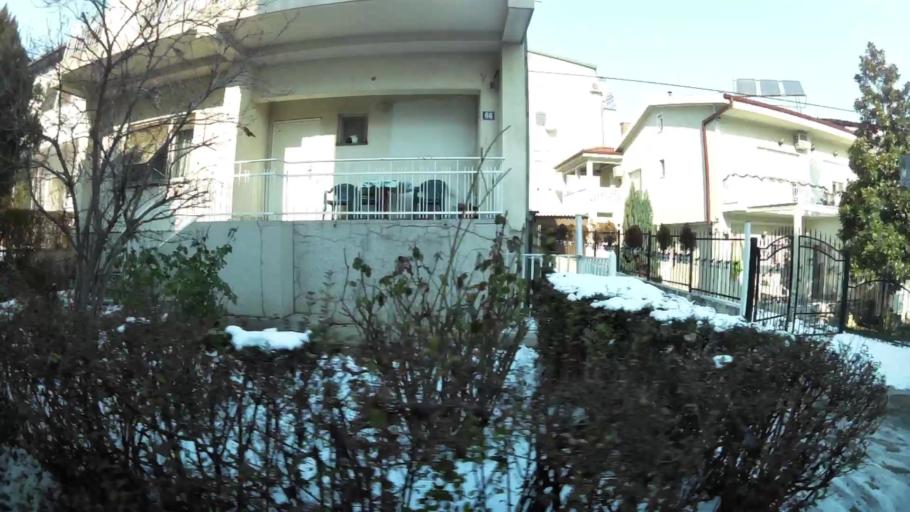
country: MK
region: Karpos
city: Skopje
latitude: 41.9822
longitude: 21.4312
